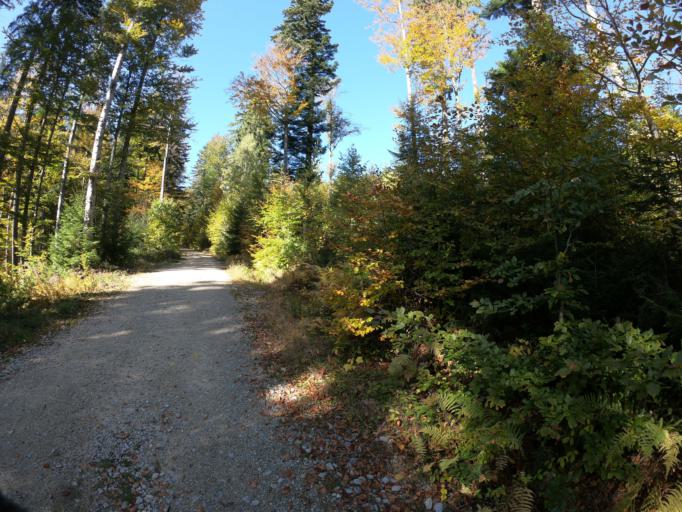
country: DE
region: Bavaria
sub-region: Lower Bavaria
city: Bayerisch Eisenstein
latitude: 49.1013
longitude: 13.1536
